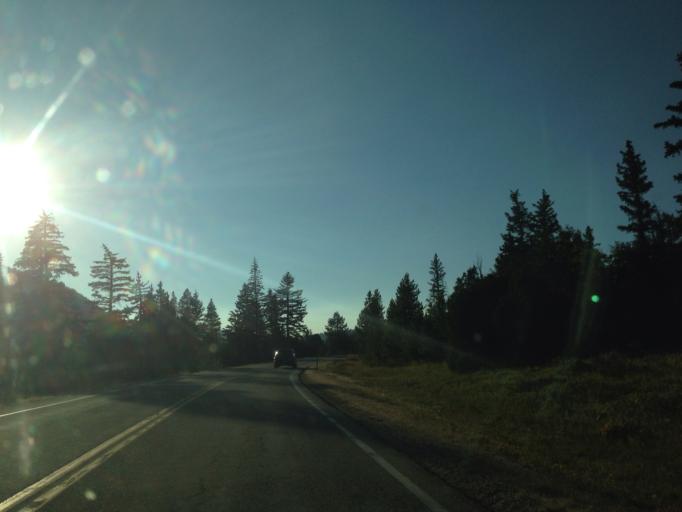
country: US
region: Utah
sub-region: Summit County
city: Francis
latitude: 40.5874
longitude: -111.0624
